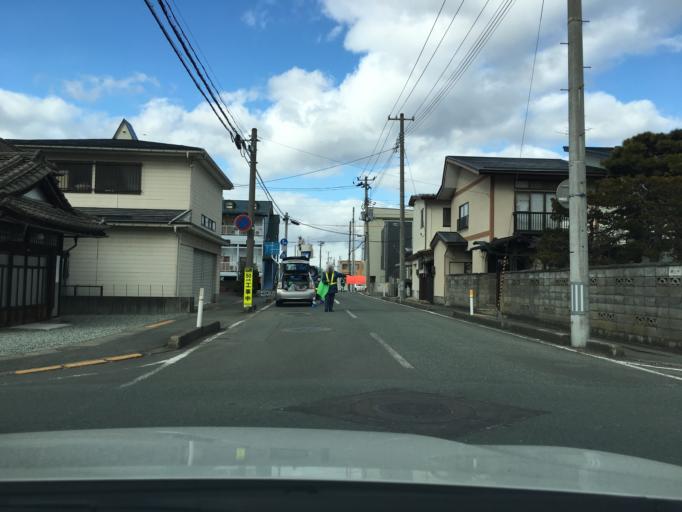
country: JP
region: Yamagata
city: Yamagata-shi
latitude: 38.2586
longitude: 140.3282
